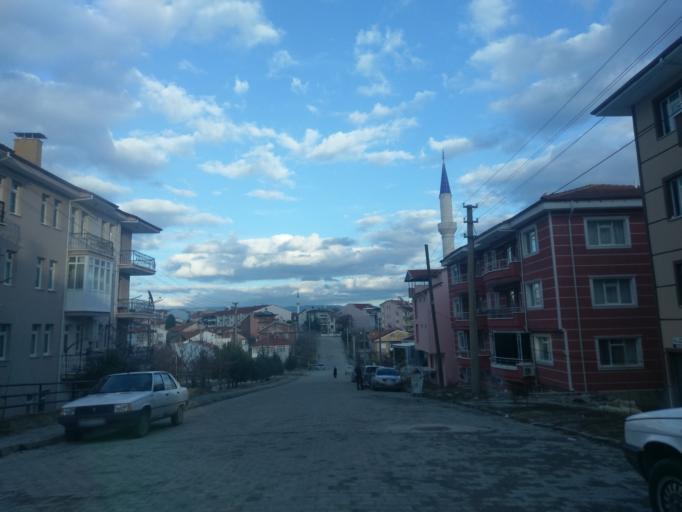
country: TR
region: Kuetahya
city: Gediz
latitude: 38.9889
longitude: 29.3822
